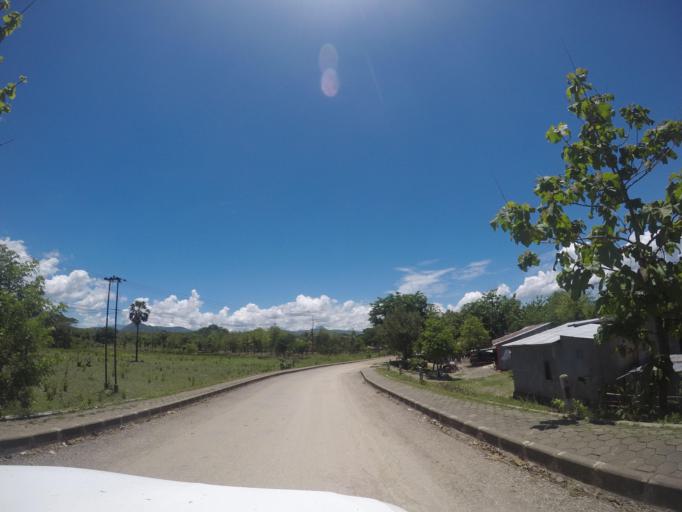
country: TL
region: Bobonaro
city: Maliana
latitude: -8.9924
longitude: 125.1939
